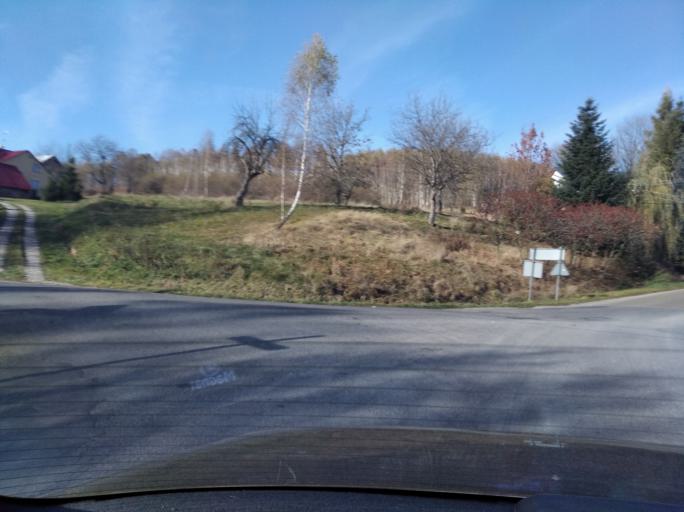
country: PL
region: Subcarpathian Voivodeship
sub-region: Powiat ropczycko-sedziszowski
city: Wielopole Skrzynskie
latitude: 49.9081
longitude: 21.5664
